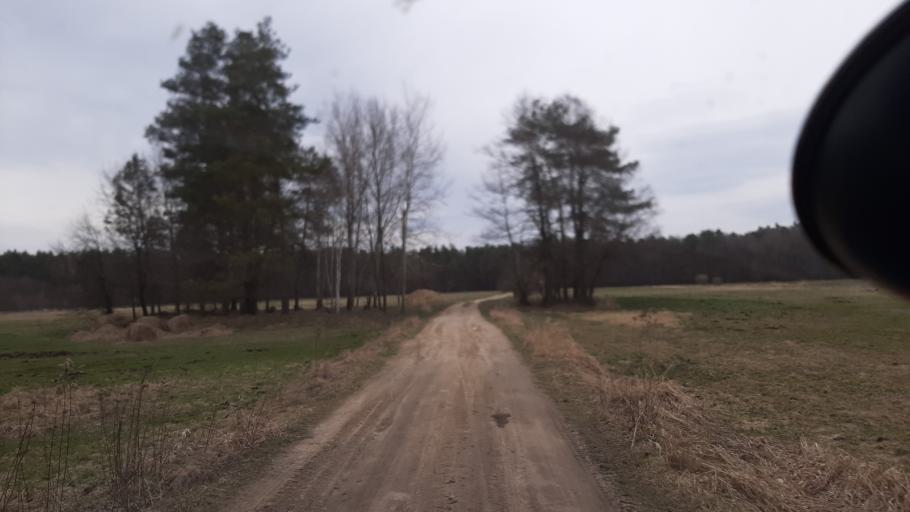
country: PL
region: Lublin Voivodeship
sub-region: Powiat lubartowski
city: Abramow
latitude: 51.4344
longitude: 22.3426
